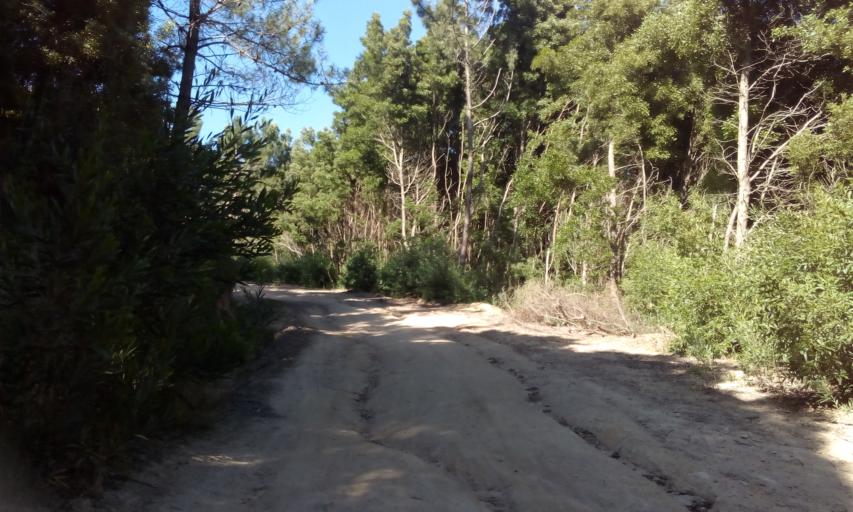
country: PT
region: Lisbon
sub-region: Sintra
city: Colares
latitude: 38.7773
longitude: -9.4357
